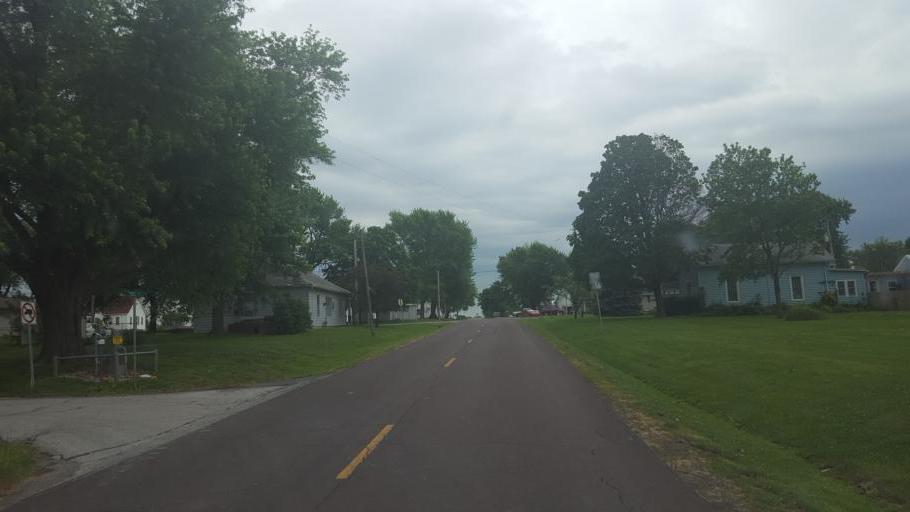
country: US
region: Missouri
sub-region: Moniteau County
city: California
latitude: 38.8113
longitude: -92.5917
